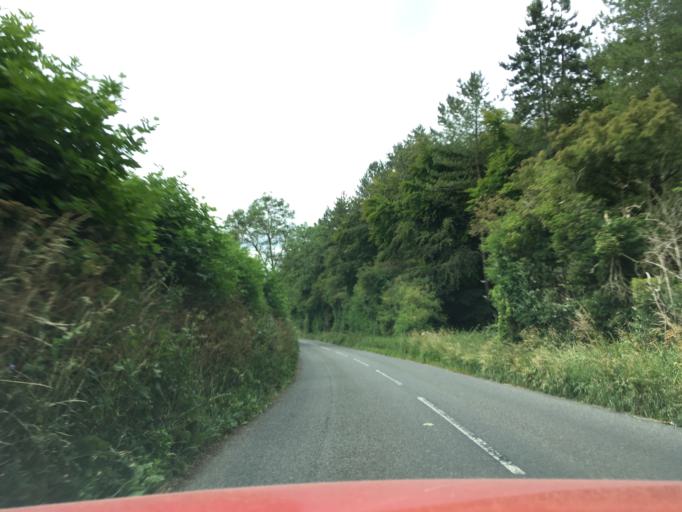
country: GB
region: England
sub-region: Oxfordshire
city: Charlbury
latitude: 51.9042
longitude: -1.4901
